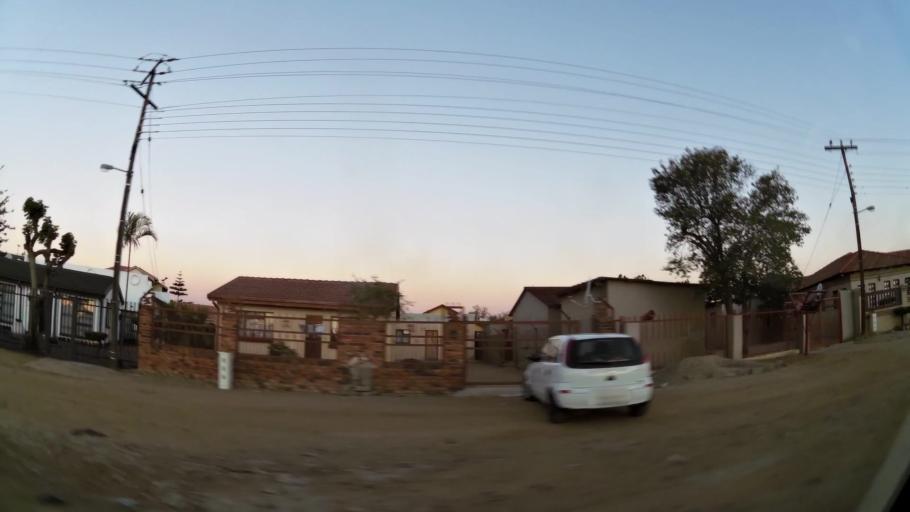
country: ZA
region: Limpopo
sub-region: Capricorn District Municipality
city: Polokwane
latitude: -23.8581
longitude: 29.3921
